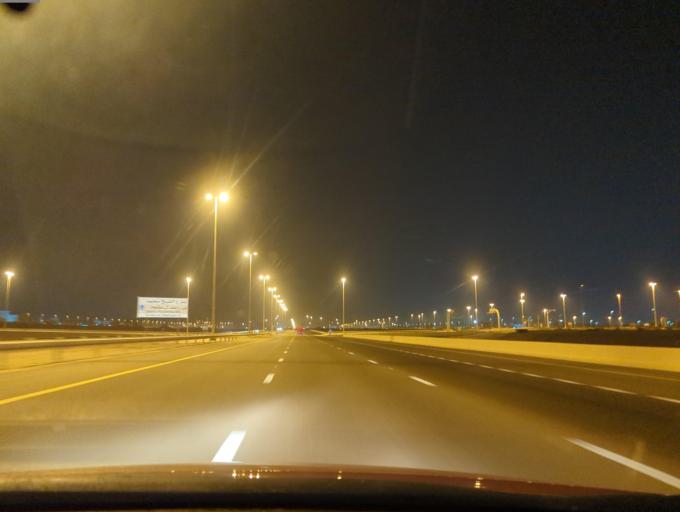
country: AE
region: Abu Dhabi
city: Abu Dhabi
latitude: 24.3921
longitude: 54.7441
